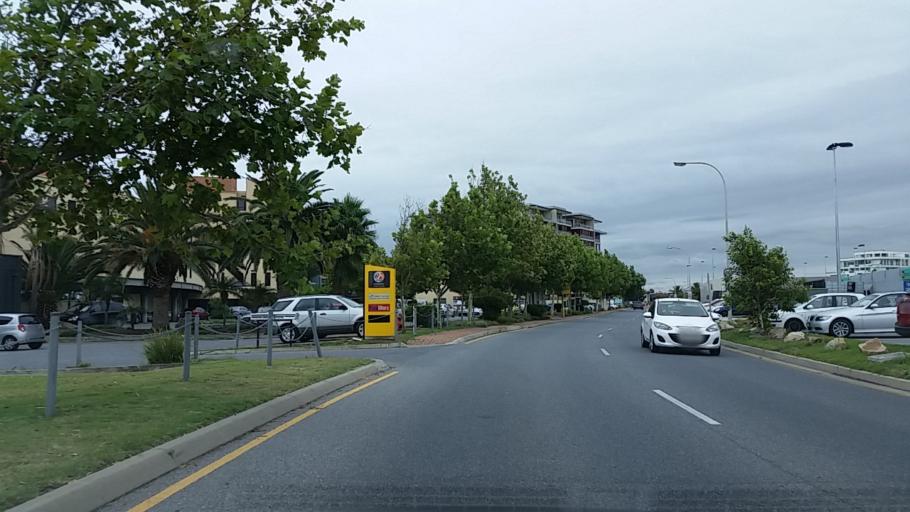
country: AU
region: South Australia
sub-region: Charles Sturt
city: West Lakes Shore
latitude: -34.8811
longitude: 138.4893
